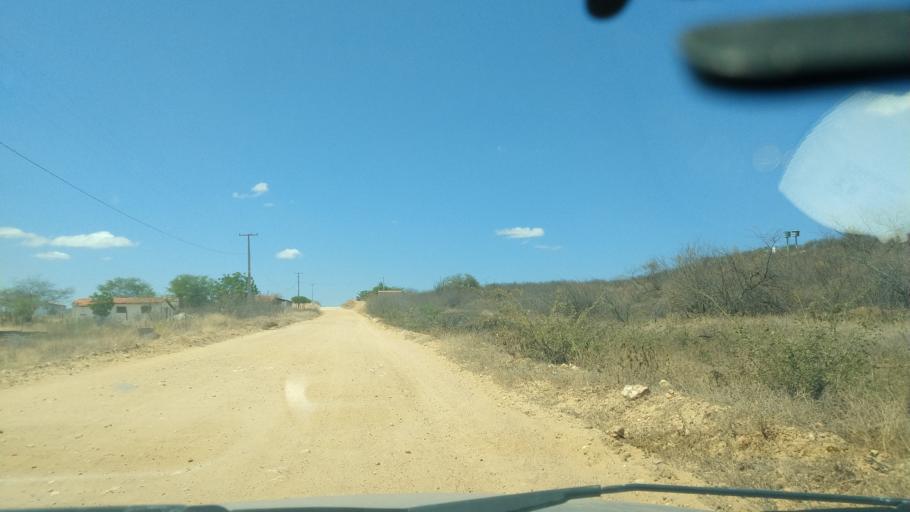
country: BR
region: Rio Grande do Norte
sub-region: Sao Tome
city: Sao Tome
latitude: -5.9804
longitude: -36.1759
